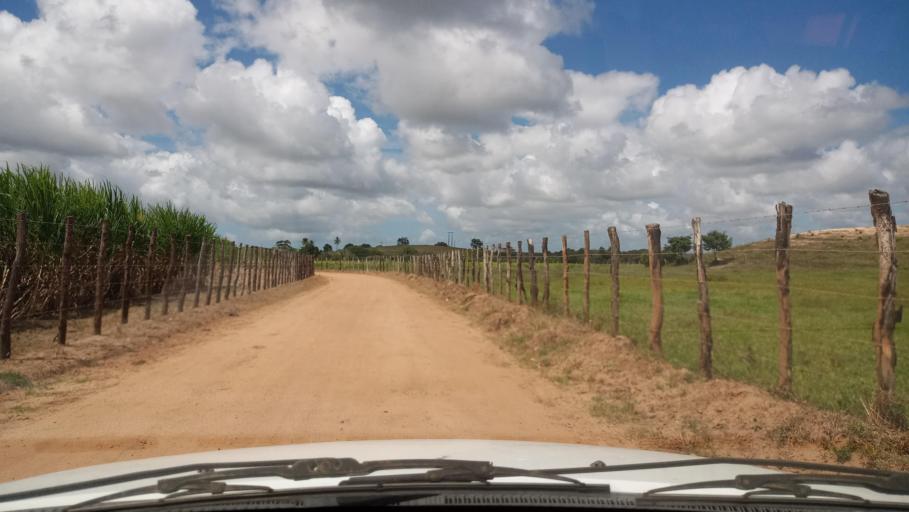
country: BR
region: Rio Grande do Norte
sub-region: Goianinha
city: Goianinha
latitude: -6.2612
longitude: -35.2434
